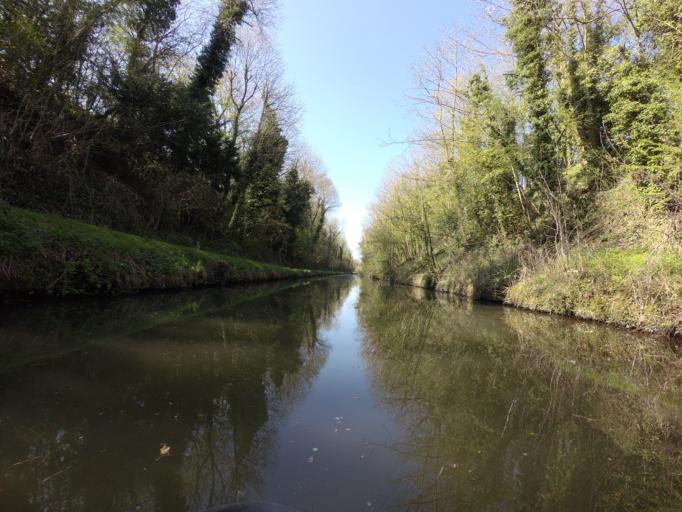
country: GB
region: England
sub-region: Hertfordshire
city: Tring
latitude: 51.8074
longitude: -0.6397
